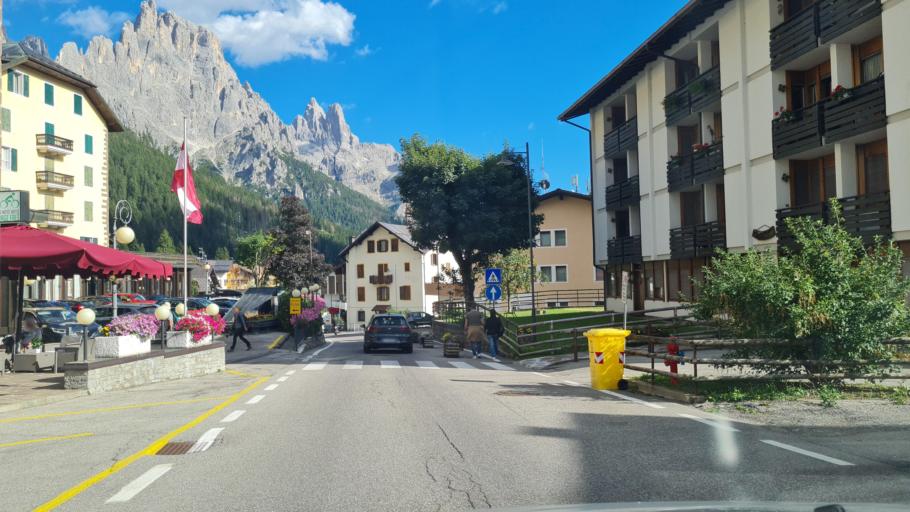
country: IT
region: Trentino-Alto Adige
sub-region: Provincia di Trento
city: Siror
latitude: 46.2635
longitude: 11.8025
